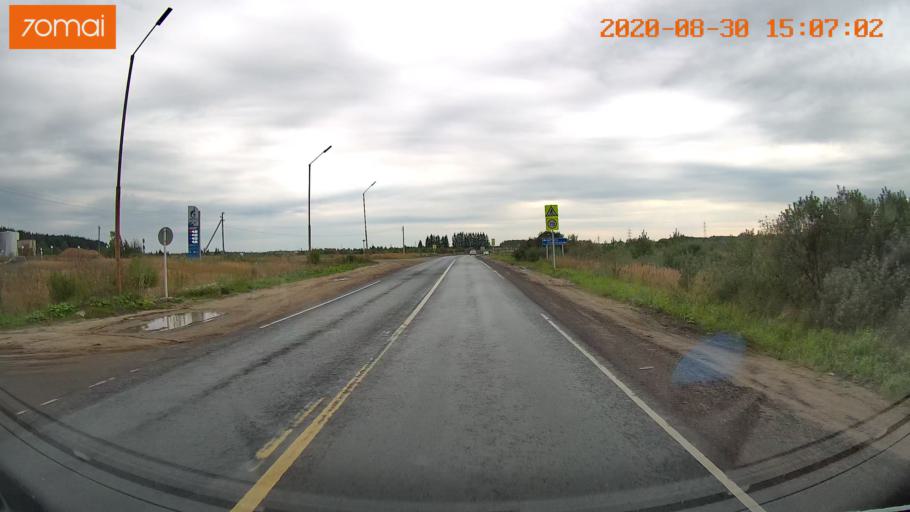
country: RU
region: Ivanovo
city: Staraya Vichuga
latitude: 57.2506
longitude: 41.8991
